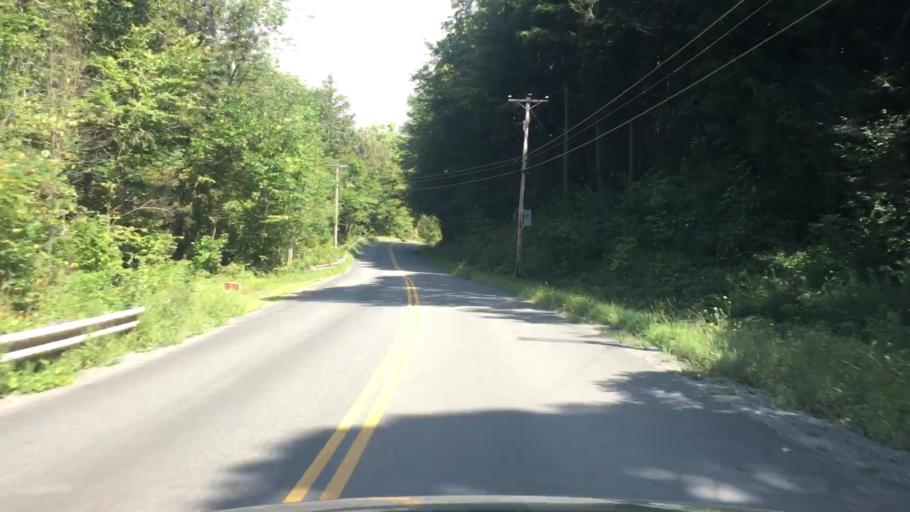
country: US
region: Vermont
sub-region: Windham County
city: West Brattleboro
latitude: 42.7986
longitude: -72.6205
